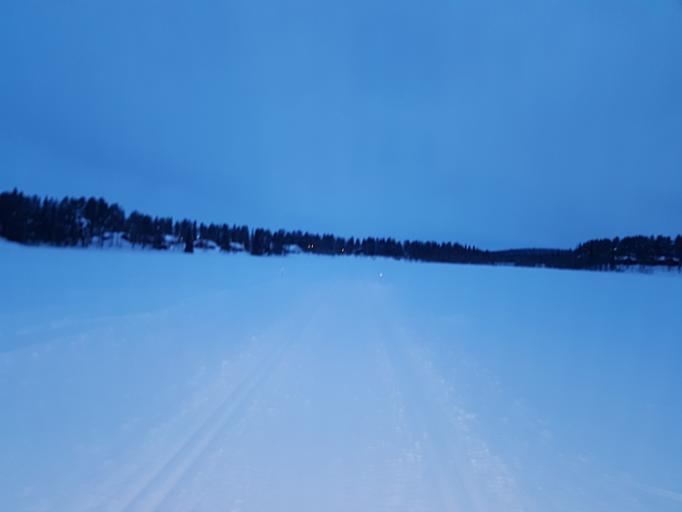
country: FI
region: Lapland
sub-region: Tunturi-Lappi
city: Kolari
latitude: 67.6090
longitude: 24.1435
